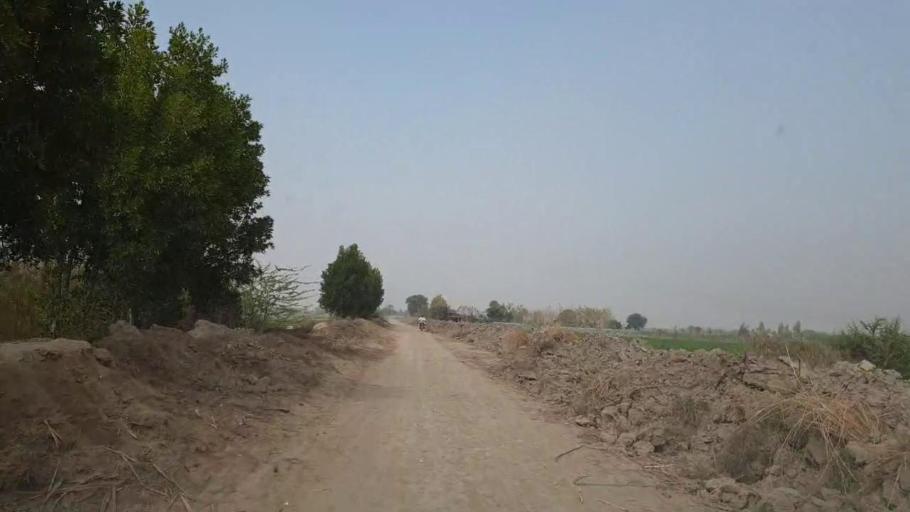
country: PK
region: Sindh
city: Mirpur Khas
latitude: 25.5626
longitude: 69.1436
